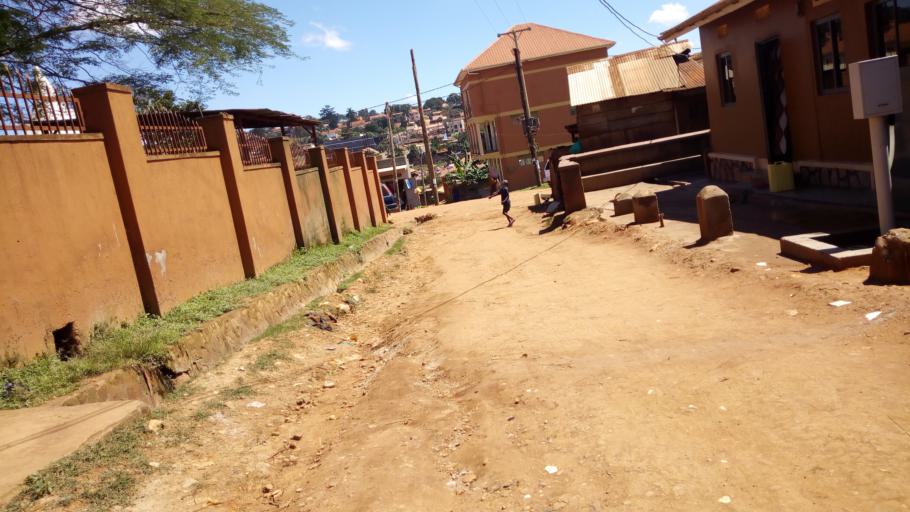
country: UG
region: Central Region
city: Kampala Central Division
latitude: 0.3579
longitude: 32.5587
